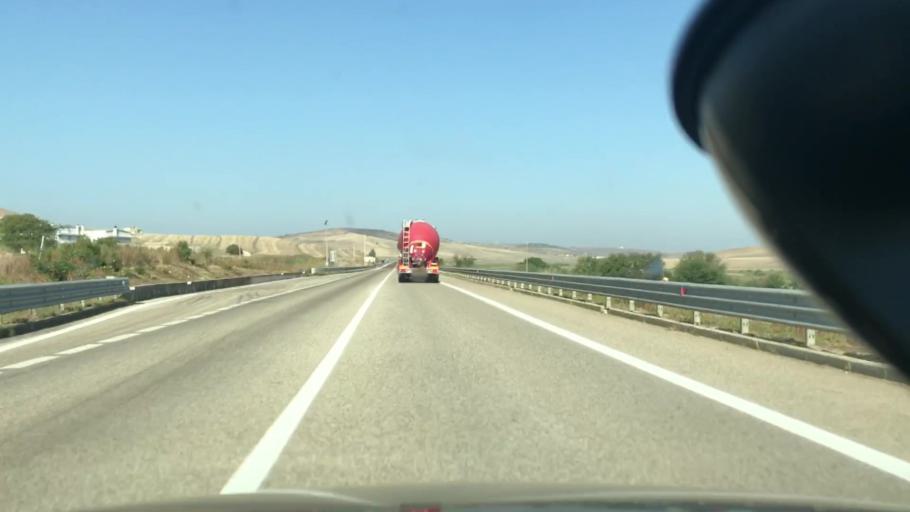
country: IT
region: Basilicate
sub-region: Provincia di Matera
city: Irsina
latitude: 40.7843
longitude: 16.3013
